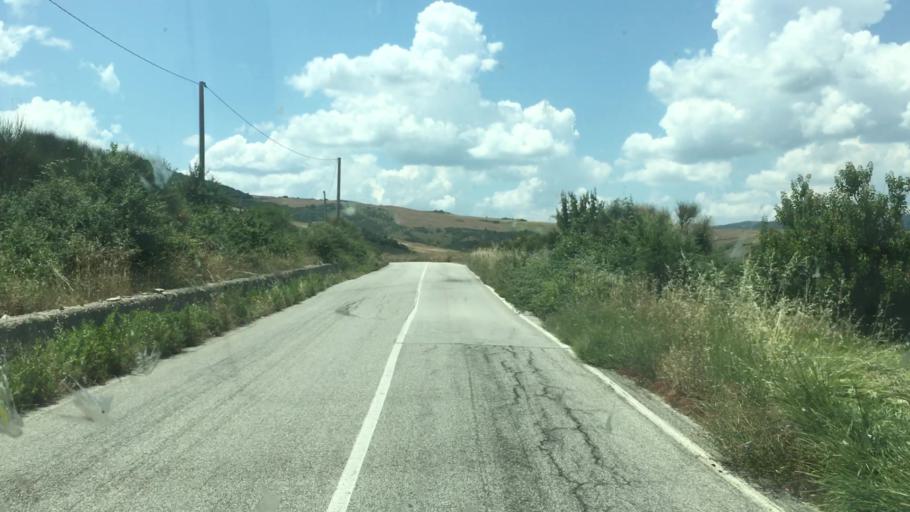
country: IT
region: Basilicate
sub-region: Provincia di Potenza
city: Tolve
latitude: 40.6978
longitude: 15.9947
